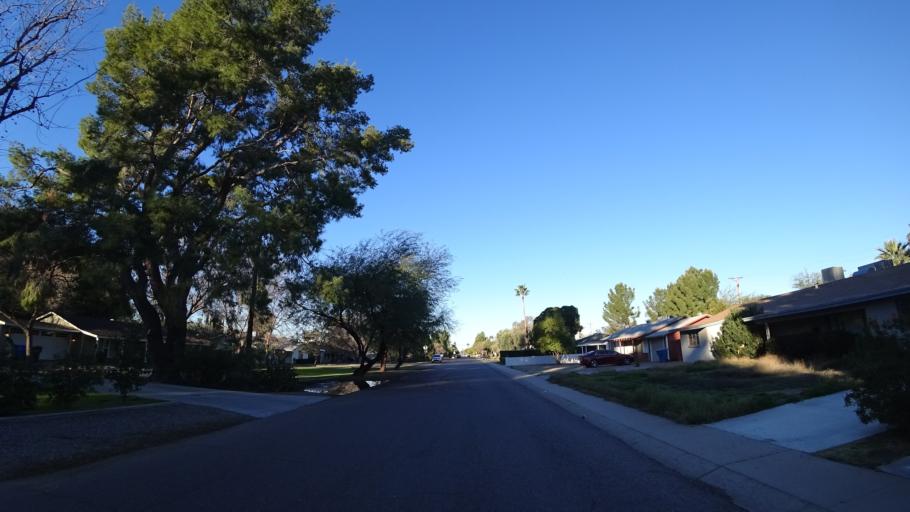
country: US
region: Arizona
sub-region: Maricopa County
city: Phoenix
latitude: 33.4915
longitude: -112.0112
